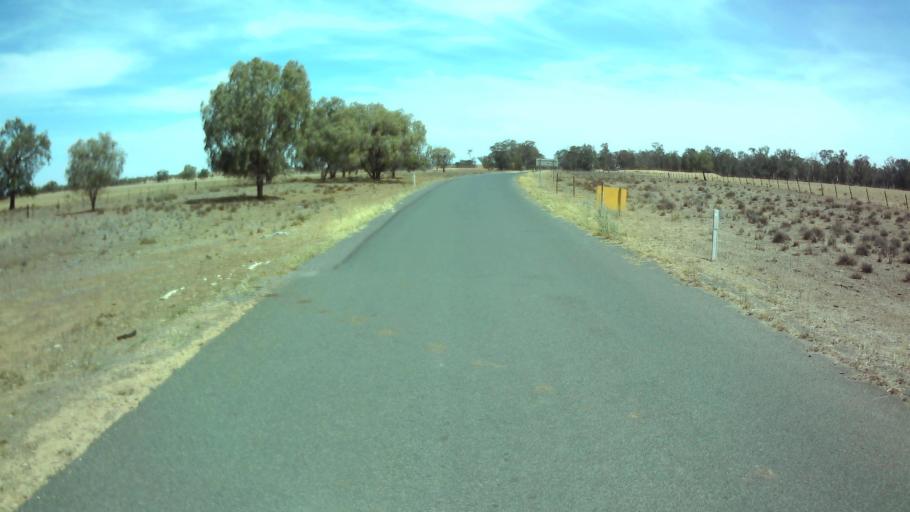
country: AU
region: New South Wales
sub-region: Weddin
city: Grenfell
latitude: -33.8597
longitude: 147.7467
